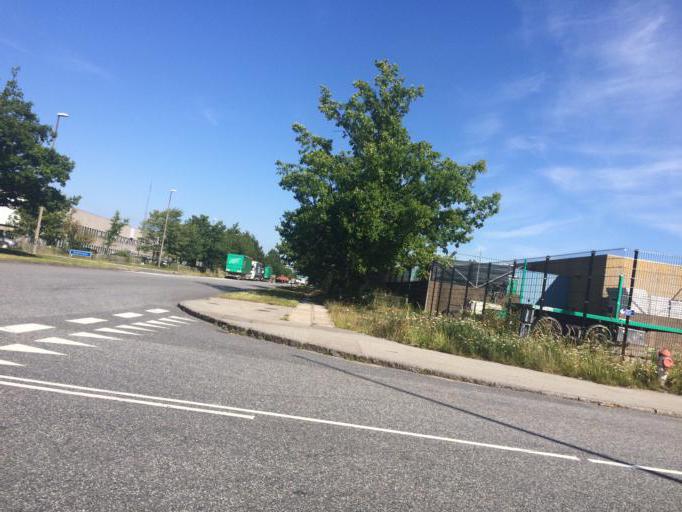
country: DK
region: Capital Region
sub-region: Hvidovre Kommune
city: Hvidovre
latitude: 55.6072
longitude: 12.4741
